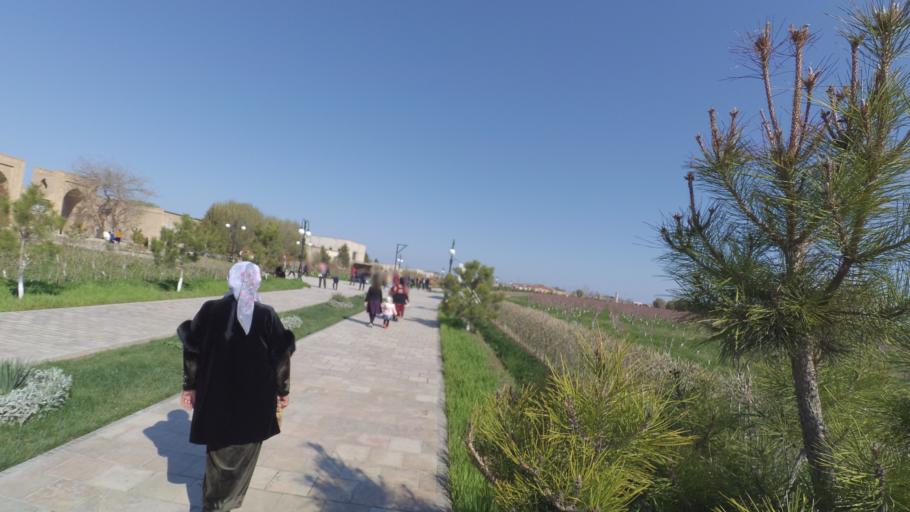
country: UZ
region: Bukhara
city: Kogon
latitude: 39.8015
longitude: 64.5387
